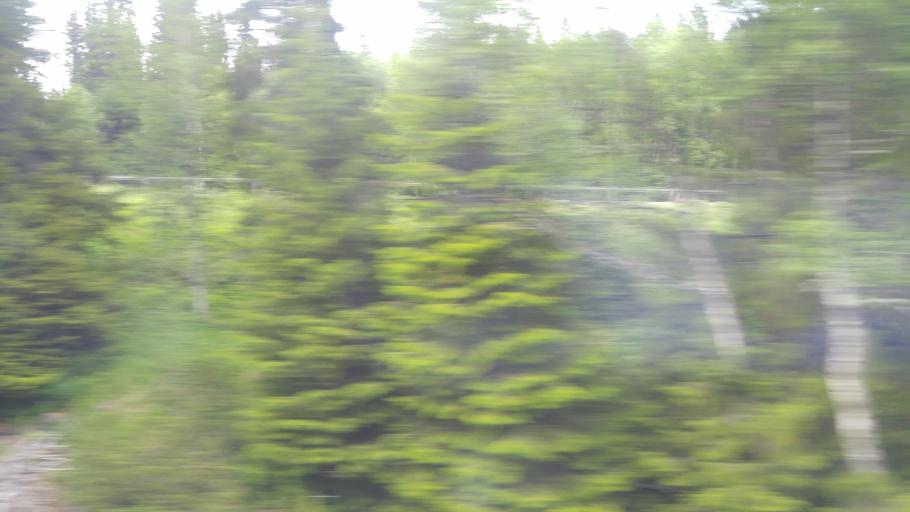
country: SE
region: Jaemtland
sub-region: Are Kommun
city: Are
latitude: 63.3815
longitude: 12.7540
